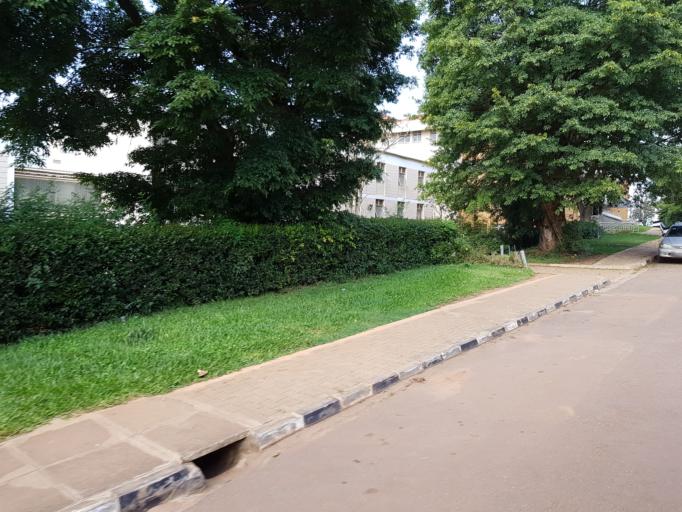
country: UG
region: Central Region
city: Kampala Central Division
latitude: 0.3330
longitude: 32.5683
